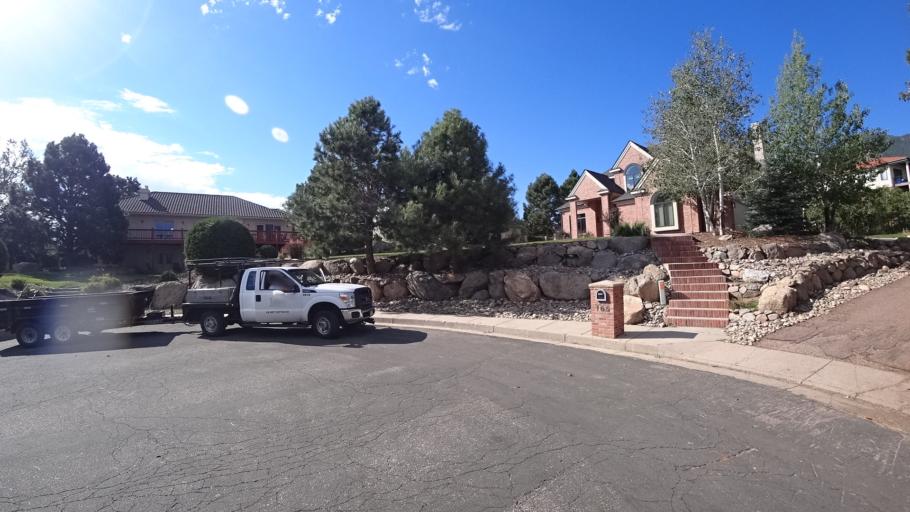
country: US
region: Colorado
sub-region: El Paso County
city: Stratmoor
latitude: 38.7688
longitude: -104.8288
